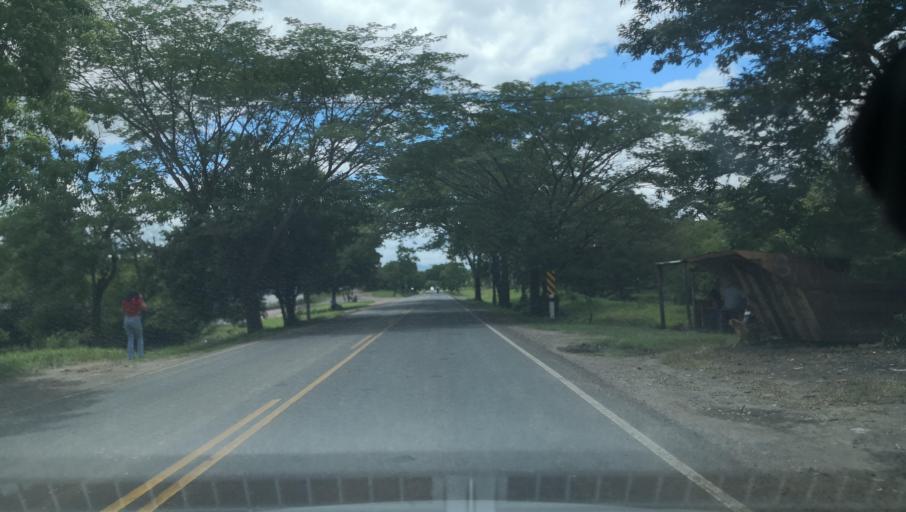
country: NI
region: Esteli
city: Esteli
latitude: 13.1626
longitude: -86.3687
